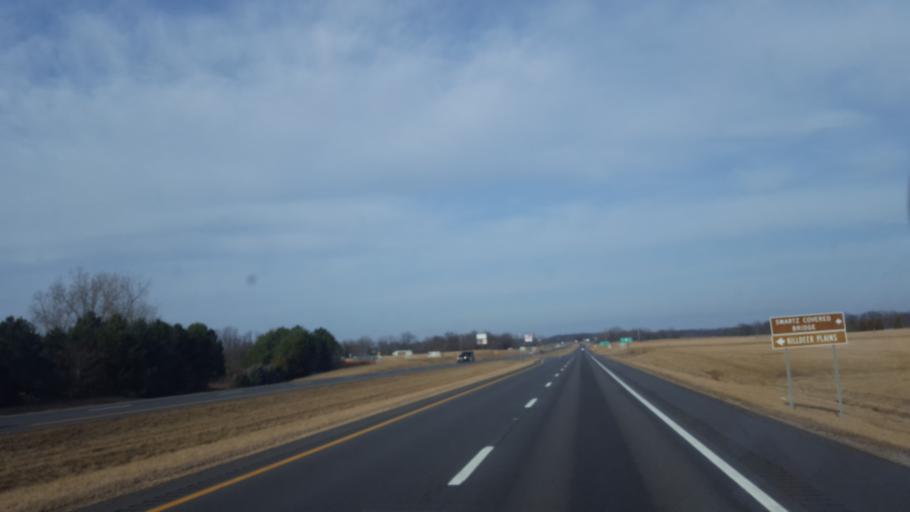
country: US
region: Ohio
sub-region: Wyandot County
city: Upper Sandusky
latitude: 40.7370
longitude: -83.2072
